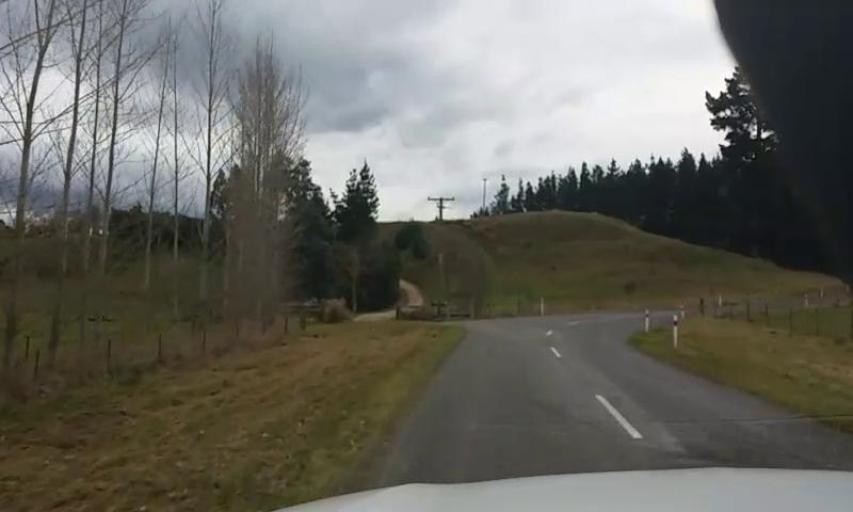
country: NZ
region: Canterbury
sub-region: Waimakariri District
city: Kaiapoi
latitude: -43.2991
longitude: 172.4377
